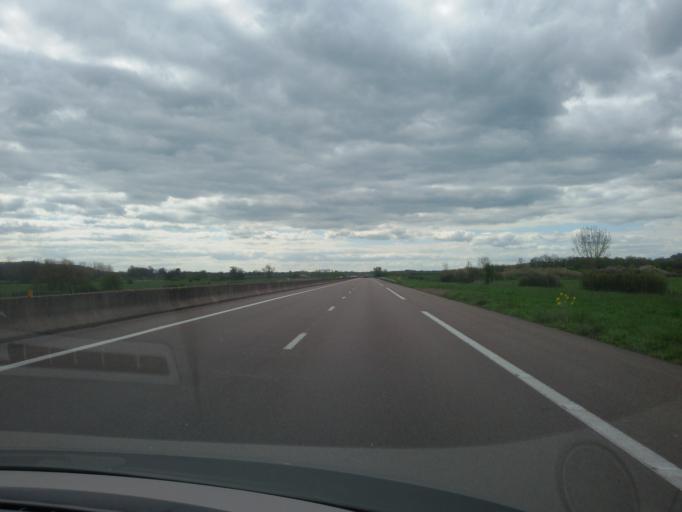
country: FR
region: Bourgogne
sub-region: Departement de la Cote-d'Or
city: Pouilly-en-Auxois
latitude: 47.2820
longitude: 4.5093
